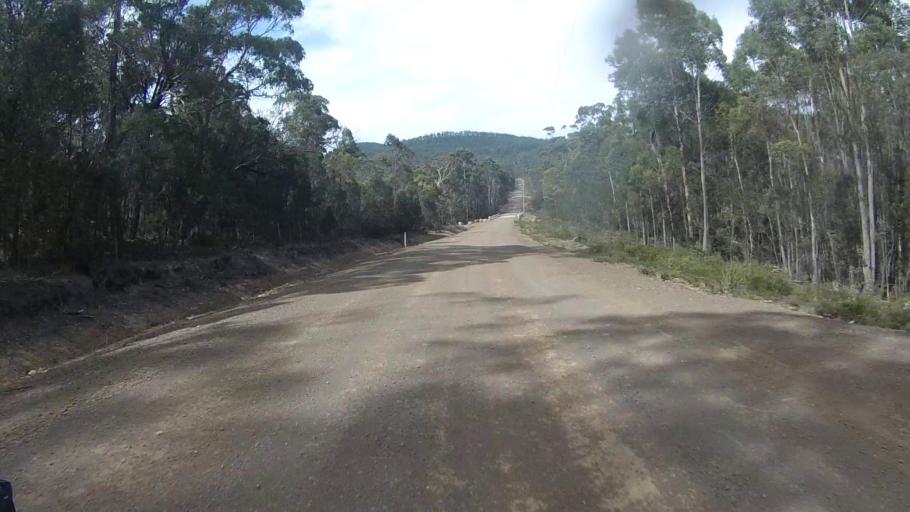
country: AU
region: Tasmania
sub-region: Sorell
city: Sorell
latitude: -42.6774
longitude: 147.8834
